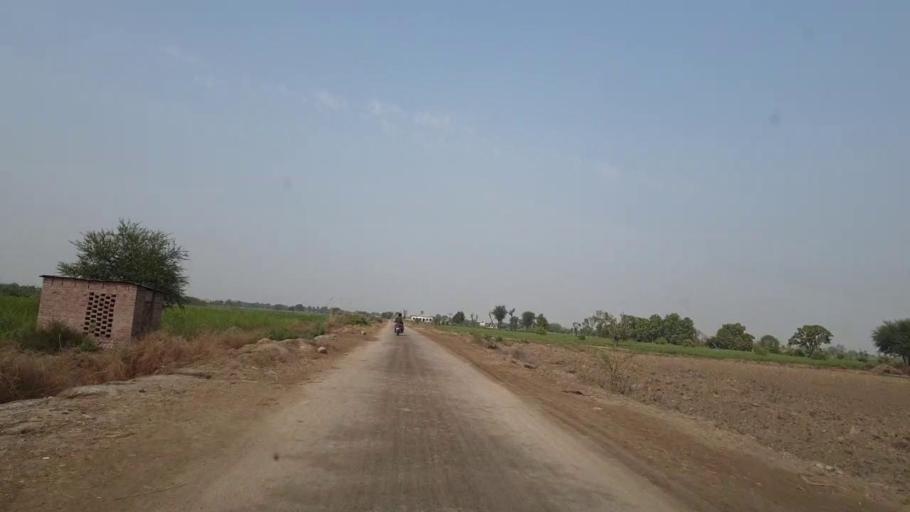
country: PK
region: Sindh
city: Mirpur Khas
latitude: 25.5617
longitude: 69.1525
